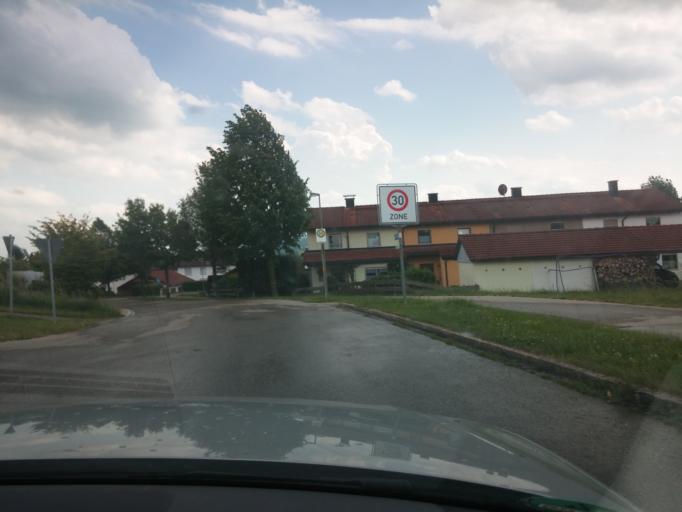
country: DE
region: Bavaria
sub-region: Swabia
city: Altusried
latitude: 47.8088
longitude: 10.2096
